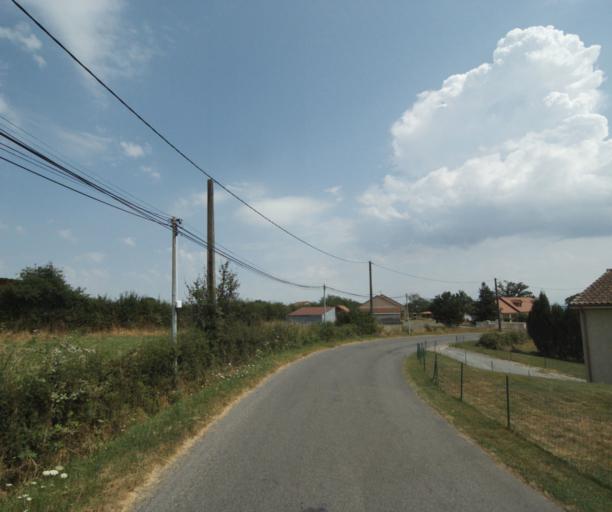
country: FR
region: Bourgogne
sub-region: Departement de Saone-et-Loire
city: Gueugnon
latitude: 46.5979
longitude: 4.0235
